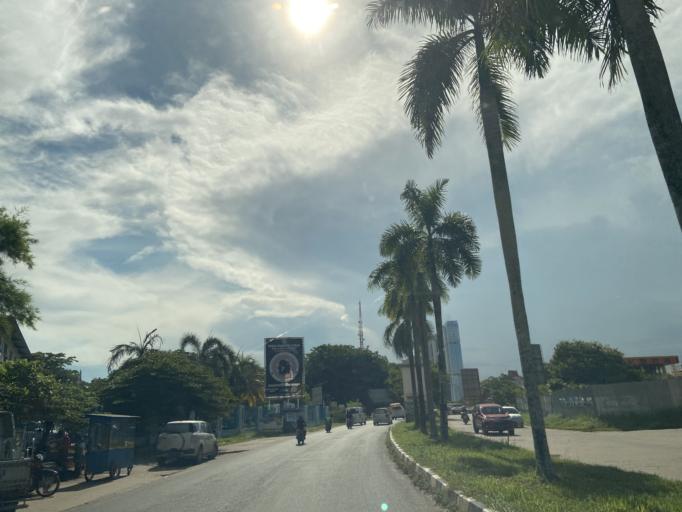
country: SG
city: Singapore
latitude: 1.1146
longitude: 104.0518
